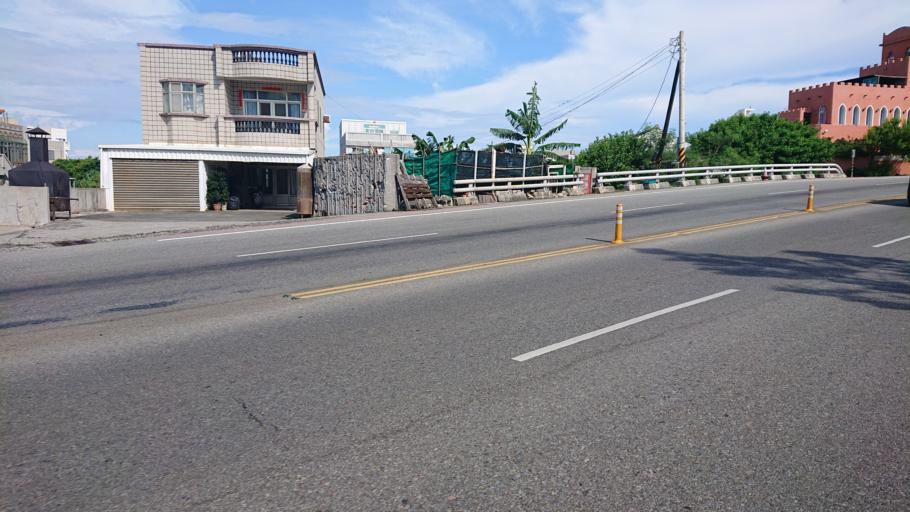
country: TW
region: Taiwan
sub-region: Penghu
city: Ma-kung
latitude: 23.5500
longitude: 119.6105
